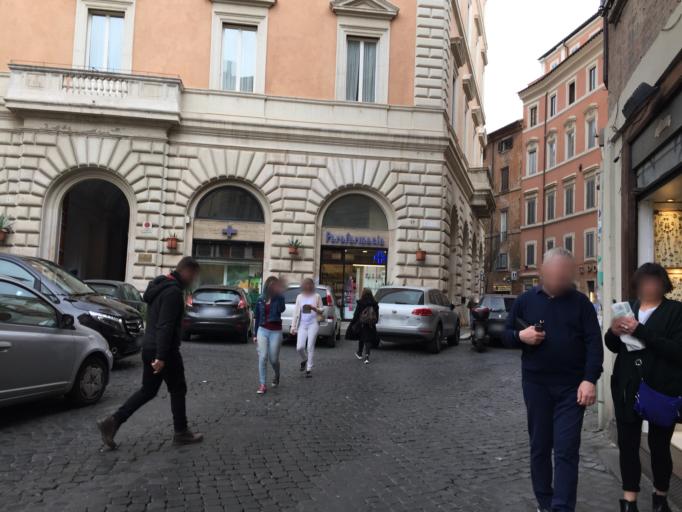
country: VA
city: Vatican City
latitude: 41.8977
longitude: 12.4783
